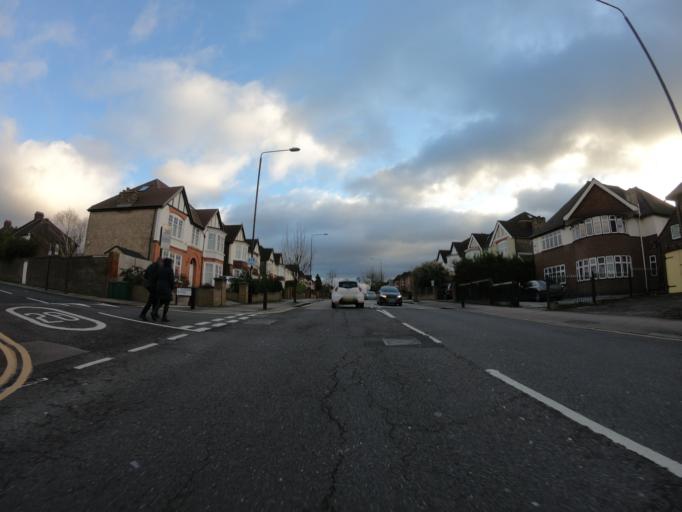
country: GB
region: England
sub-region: Greater London
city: Woolwich
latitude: 51.4545
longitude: 0.0609
